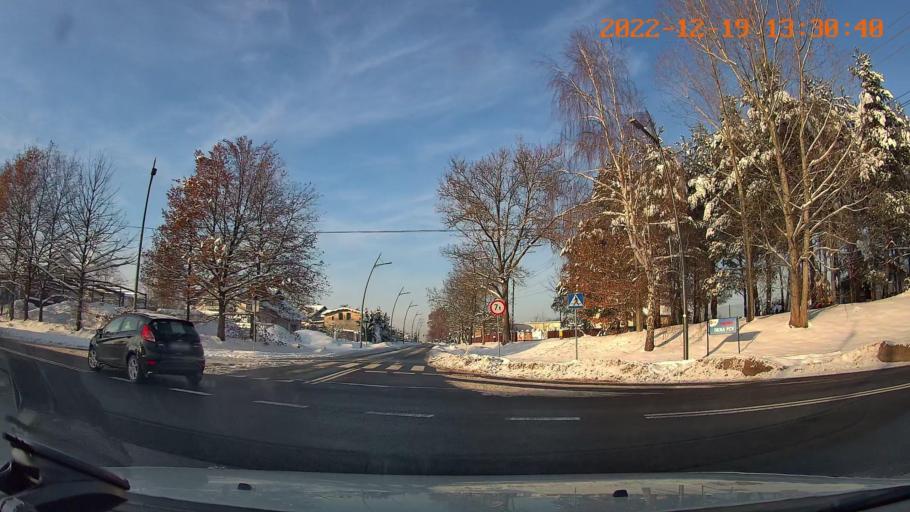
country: PL
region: Silesian Voivodeship
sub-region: Powiat bierunsko-ledzinski
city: Ledziny
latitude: 50.1196
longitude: 19.1119
